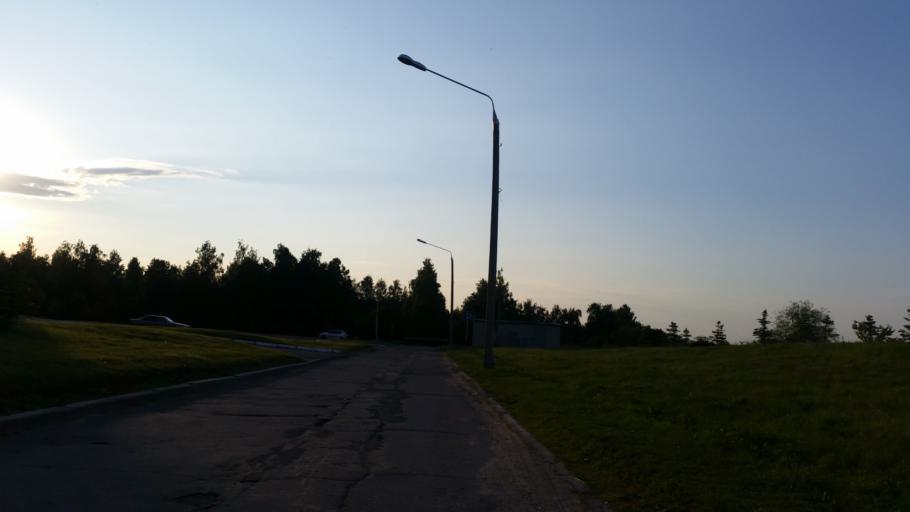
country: RU
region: Ulyanovsk
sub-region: Ulyanovskiy Rayon
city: Ulyanovsk
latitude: 54.3513
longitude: 48.3913
